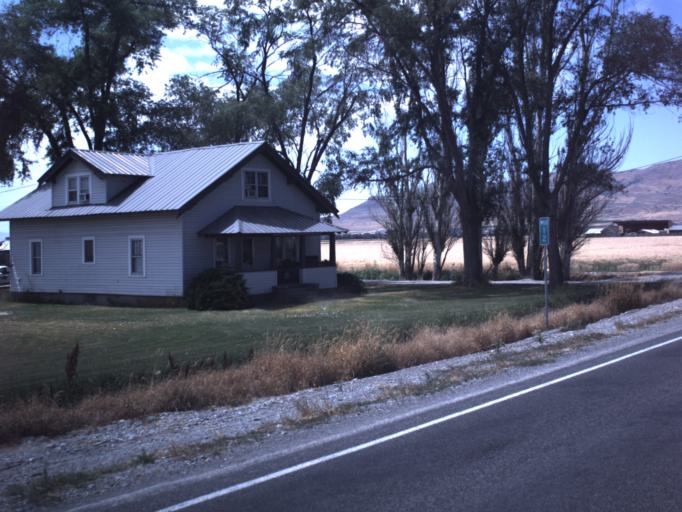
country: US
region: Utah
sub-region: Box Elder County
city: Tremonton
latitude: 41.7099
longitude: -112.2484
